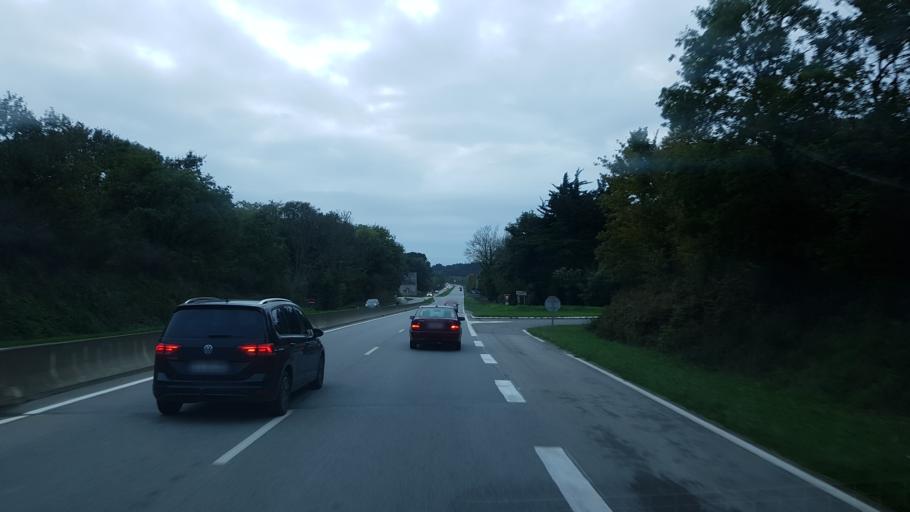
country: FR
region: Brittany
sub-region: Departement du Morbihan
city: Sarzeau
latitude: 47.5434
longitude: -2.7255
